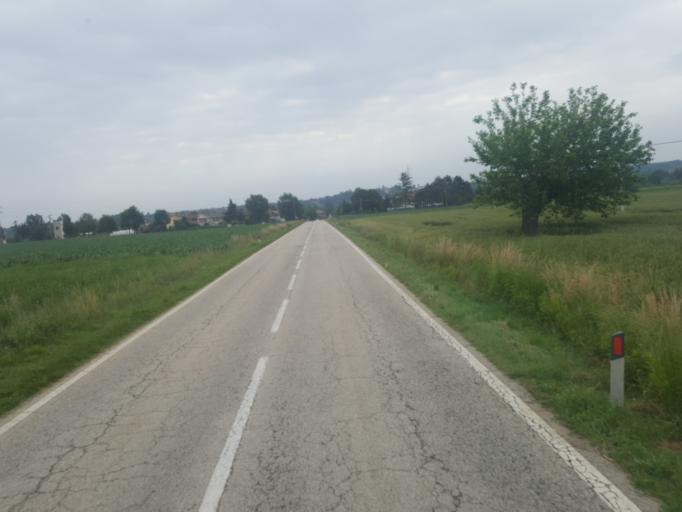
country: IT
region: Piedmont
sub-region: Provincia di Torino
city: Pralormo
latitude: 44.8564
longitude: 7.8691
